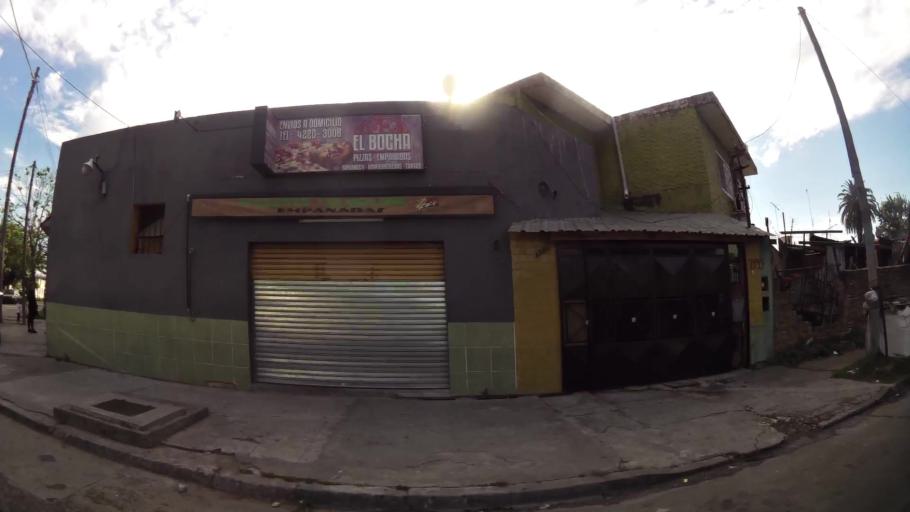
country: AR
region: Buenos Aires
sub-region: Partido de Lanus
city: Lanus
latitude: -34.7024
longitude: -58.3536
